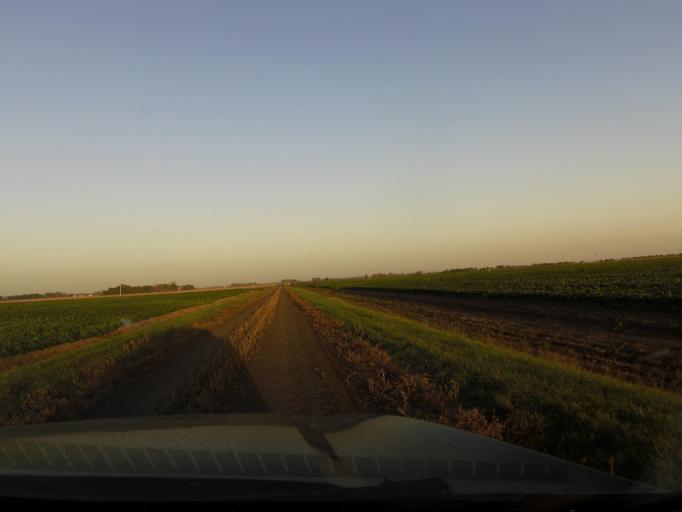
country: US
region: North Dakota
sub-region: Walsh County
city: Grafton
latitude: 48.3831
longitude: -97.2383
